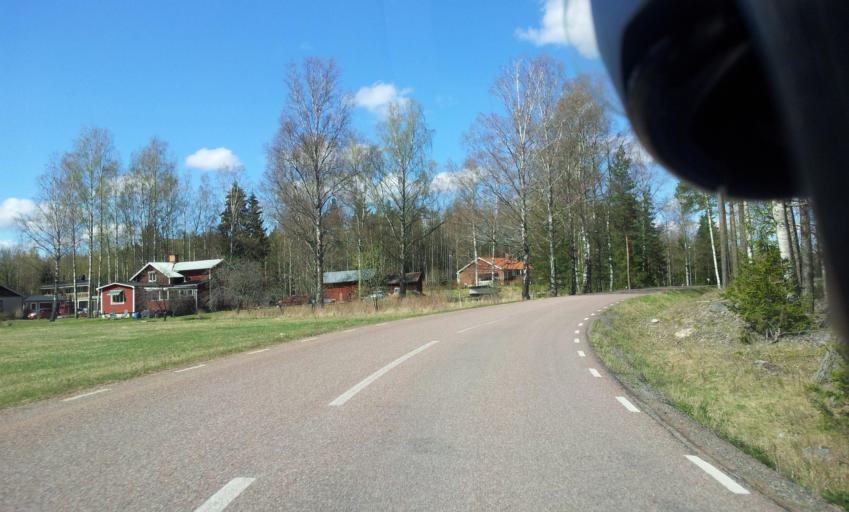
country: SE
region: Dalarna
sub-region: Borlange Kommun
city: Ornas
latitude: 60.4819
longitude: 15.5461
